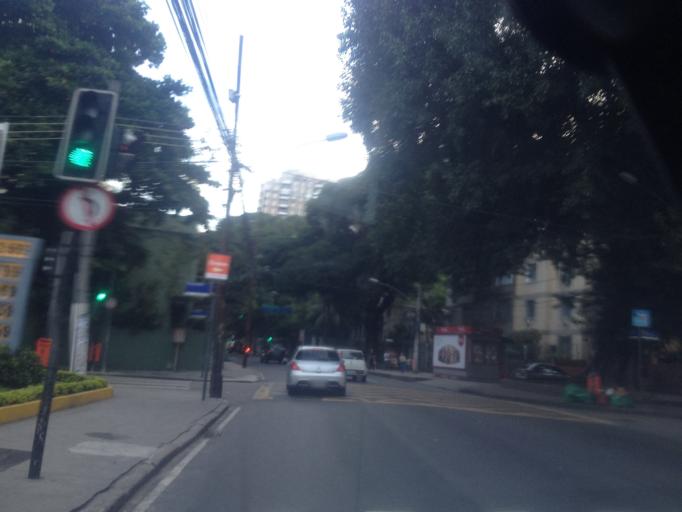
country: BR
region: Rio de Janeiro
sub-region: Rio De Janeiro
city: Rio de Janeiro
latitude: -22.9506
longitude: -43.1926
